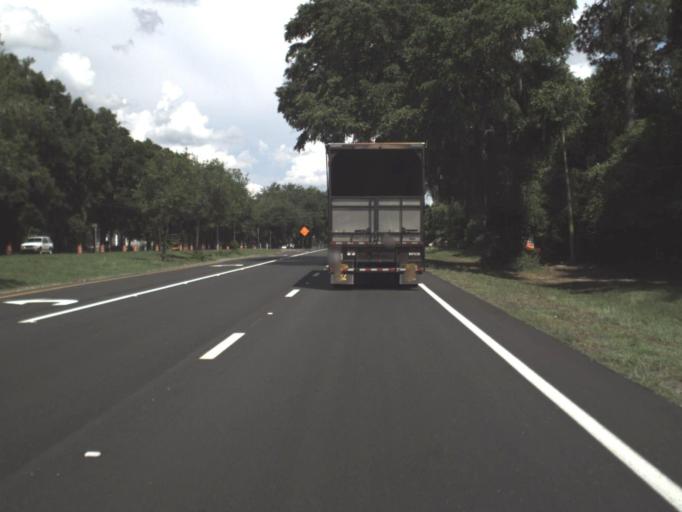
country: US
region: Florida
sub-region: Alachua County
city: Alachua
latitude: 29.7745
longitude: -82.4408
